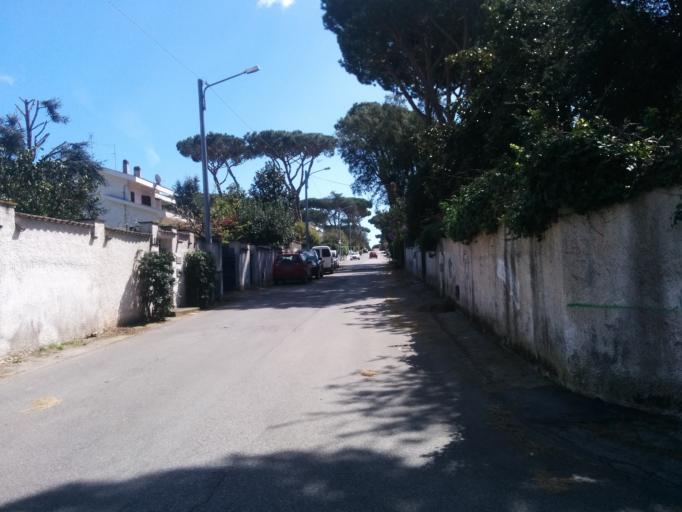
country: IT
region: Latium
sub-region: Citta metropolitana di Roma Capitale
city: Lavinio
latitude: 41.5004
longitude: 12.5960
